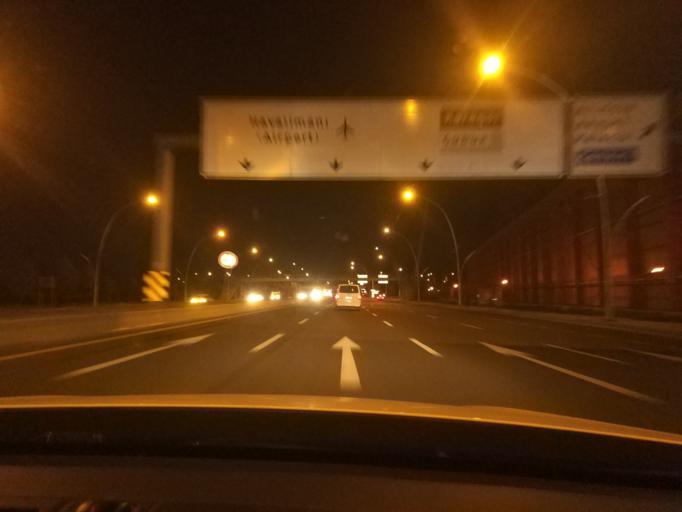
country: TR
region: Ankara
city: Akyurt
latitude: 40.0766
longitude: 32.9564
